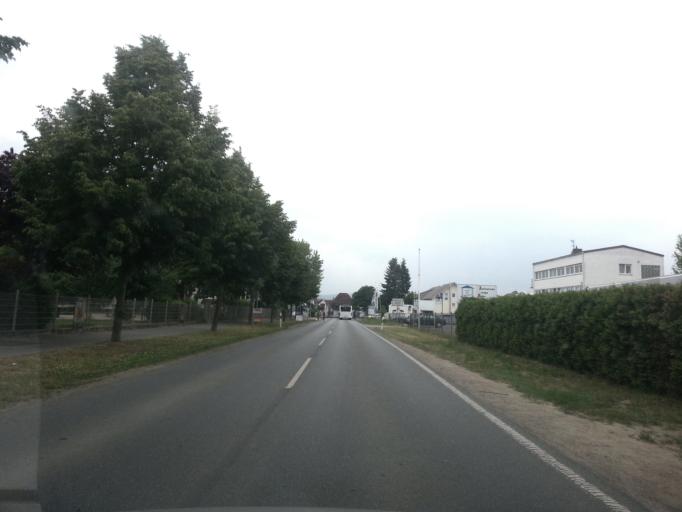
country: DE
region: Hesse
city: Pfungstadt
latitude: 49.8071
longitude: 8.5920
